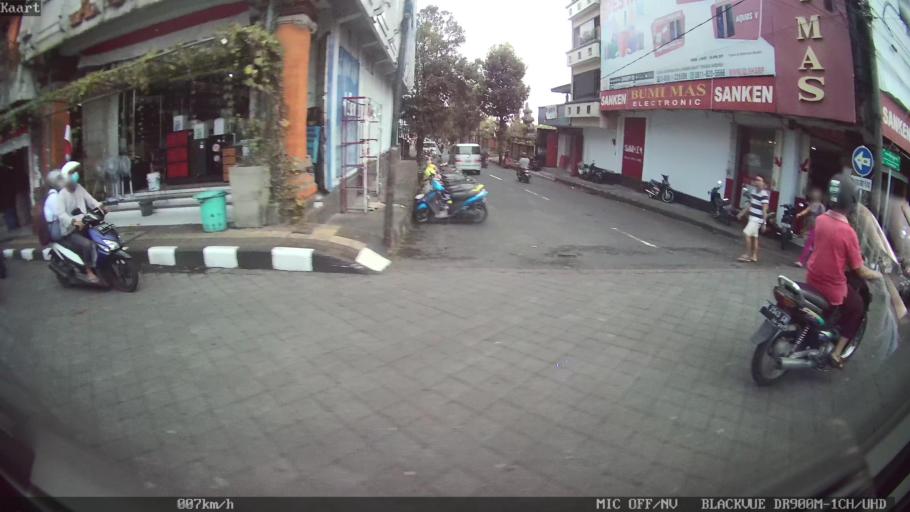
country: ID
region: Bali
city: Tabanan
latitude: -8.5393
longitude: 115.1254
